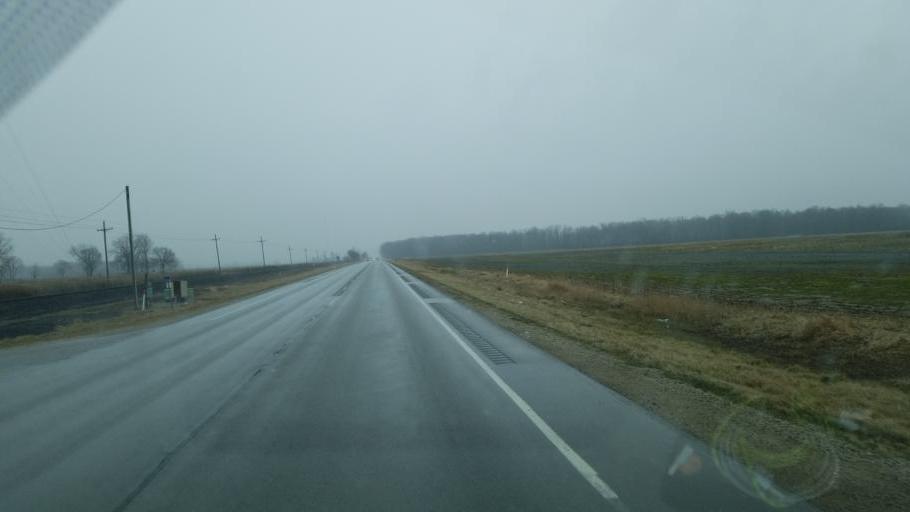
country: US
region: Indiana
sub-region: Wabash County
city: Mount Vernon
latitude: 40.7101
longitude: -85.7655
